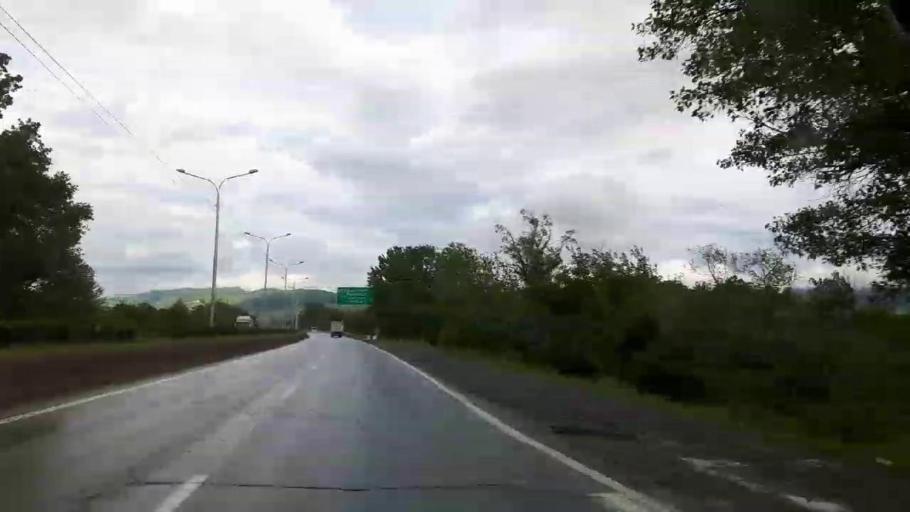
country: GE
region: Shida Kartli
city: Kaspi
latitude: 41.9119
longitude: 44.5640
